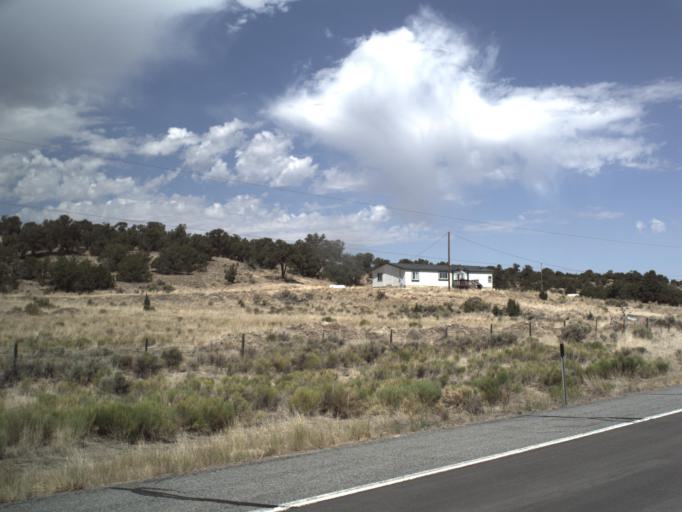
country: US
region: Utah
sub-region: Utah County
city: Eagle Mountain
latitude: 40.0250
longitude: -112.2817
